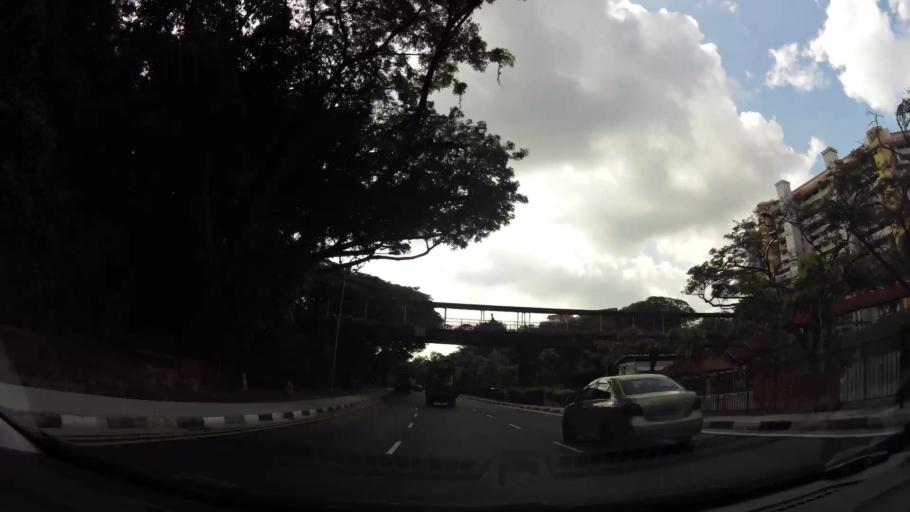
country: SG
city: Singapore
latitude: 1.2728
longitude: 103.8236
